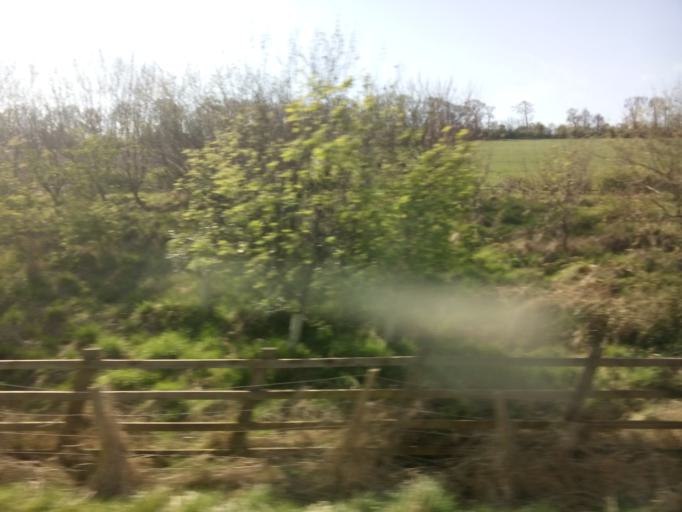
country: GB
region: Scotland
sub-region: East Lothian
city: East Linton
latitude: 55.9873
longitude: -2.6301
